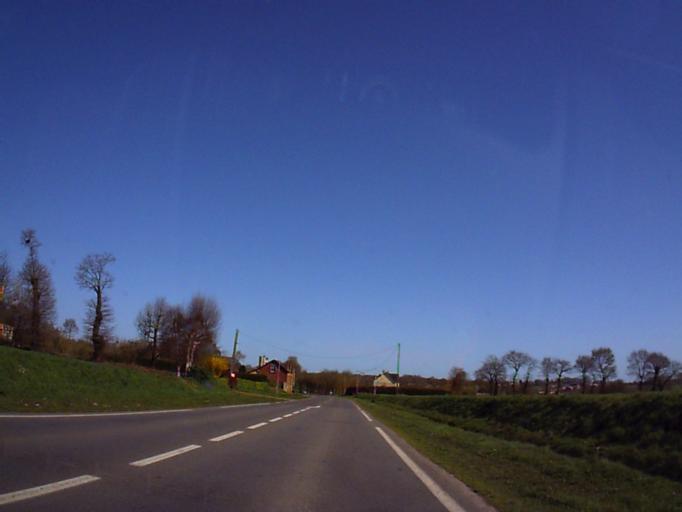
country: FR
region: Brittany
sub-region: Departement d'Ille-et-Vilaine
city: Saint-Meen-le-Grand
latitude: 48.2049
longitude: -2.1755
